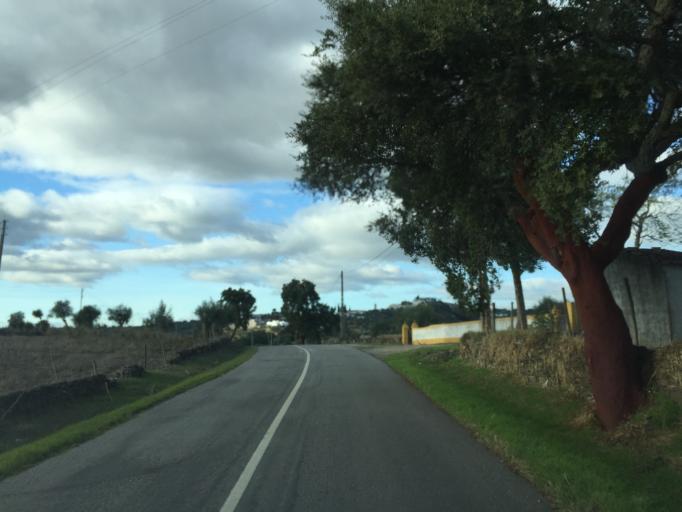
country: PT
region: Portalegre
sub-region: Alter do Chao
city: Alter do Chao
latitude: 39.2750
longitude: -7.6396
